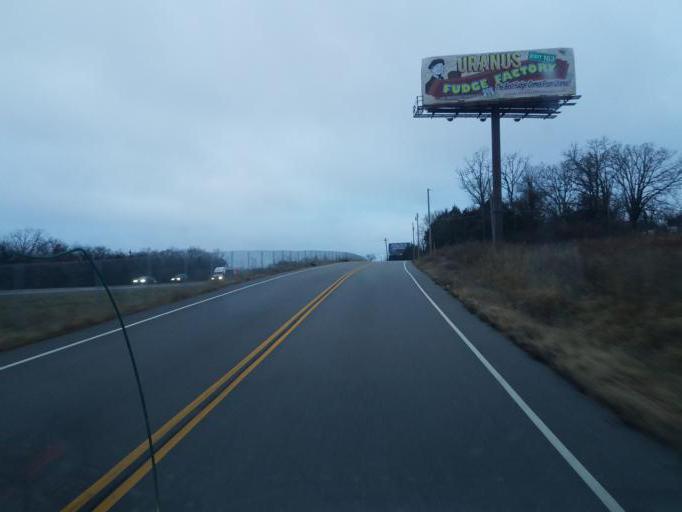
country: US
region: Missouri
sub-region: Phelps County
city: Rolla
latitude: 37.9765
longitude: -91.7409
